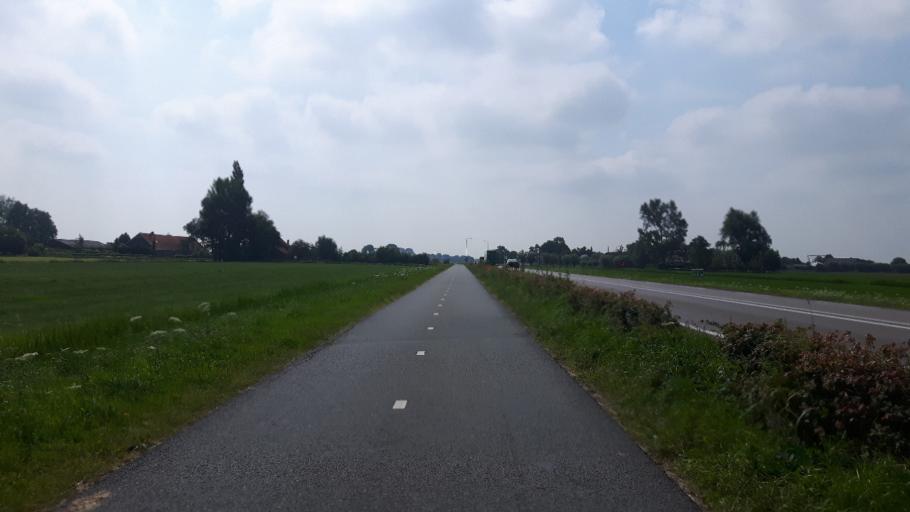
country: NL
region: Utrecht
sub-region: Gemeente Montfoort
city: Montfoort
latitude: 52.0279
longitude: 4.9445
